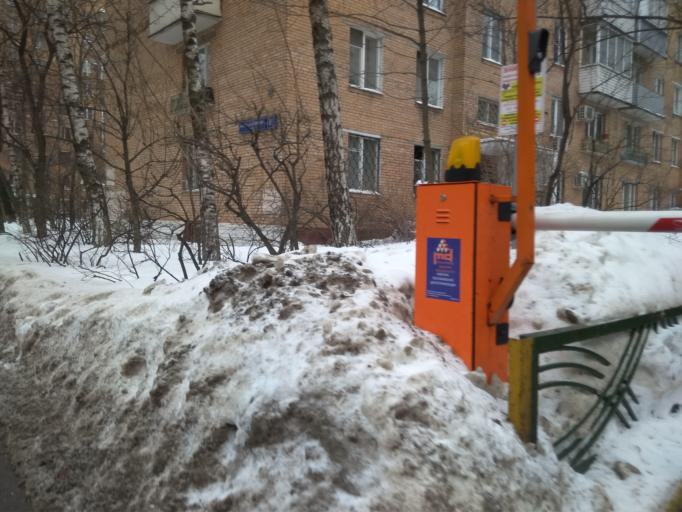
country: RU
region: Moscow
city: Sokol
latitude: 55.7922
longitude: 37.4959
